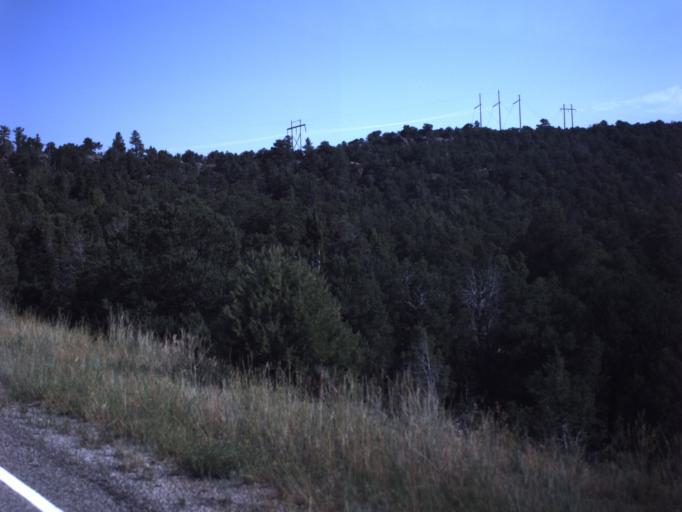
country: US
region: Utah
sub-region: Daggett County
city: Manila
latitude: 40.9148
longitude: -109.4137
